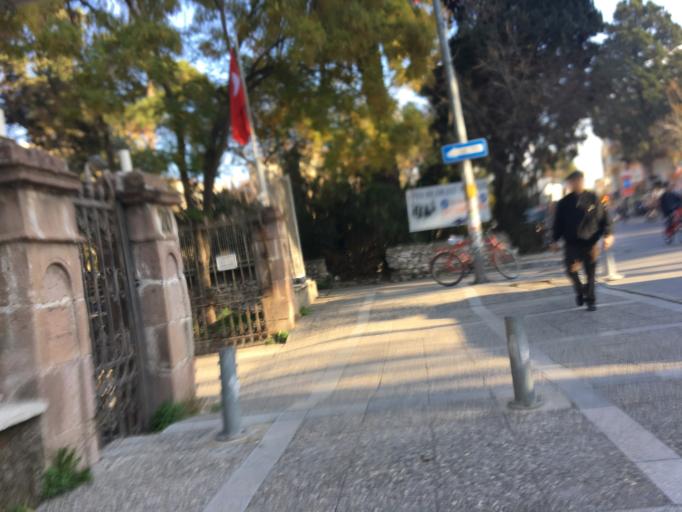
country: TR
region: Izmir
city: Buca
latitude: 38.3886
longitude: 27.1721
